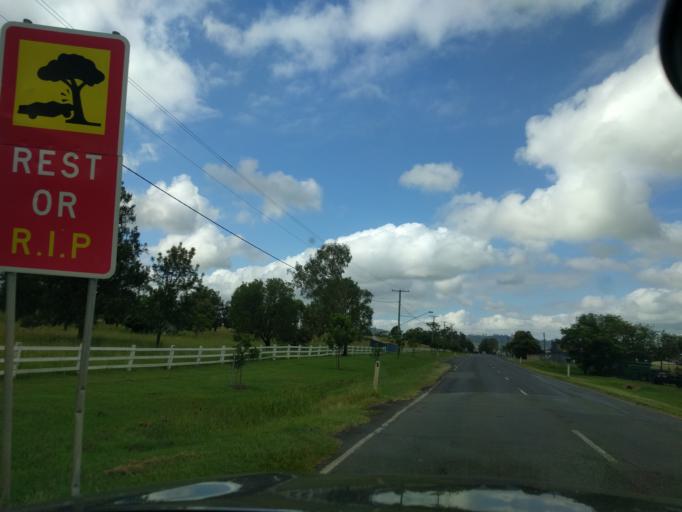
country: AU
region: Queensland
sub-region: Logan
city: Cedar Vale
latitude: -27.9967
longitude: 152.9892
